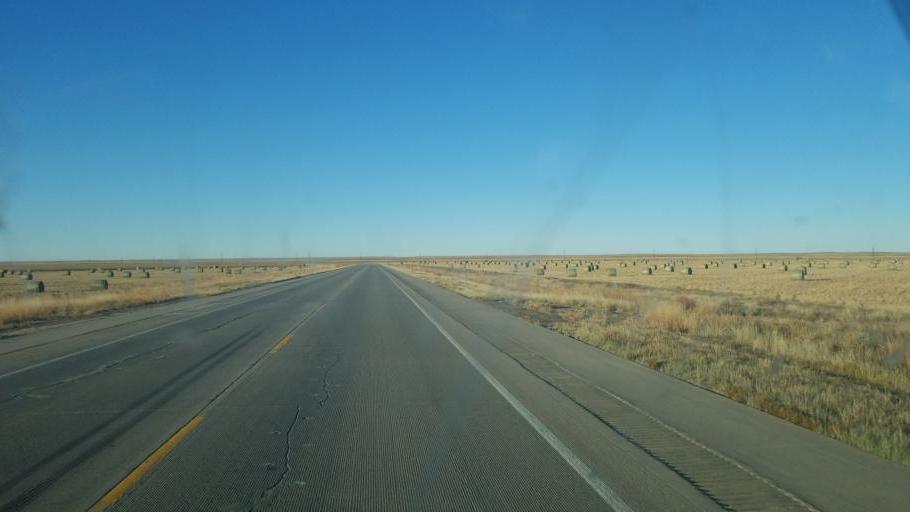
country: US
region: Colorado
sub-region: Kiowa County
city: Eads
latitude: 38.6851
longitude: -102.7790
